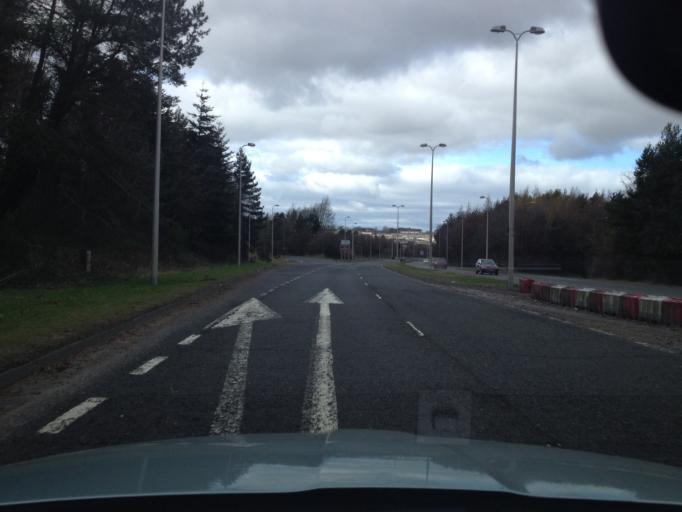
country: GB
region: Scotland
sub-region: West Lothian
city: Mid Calder
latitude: 55.8845
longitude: -3.4972
